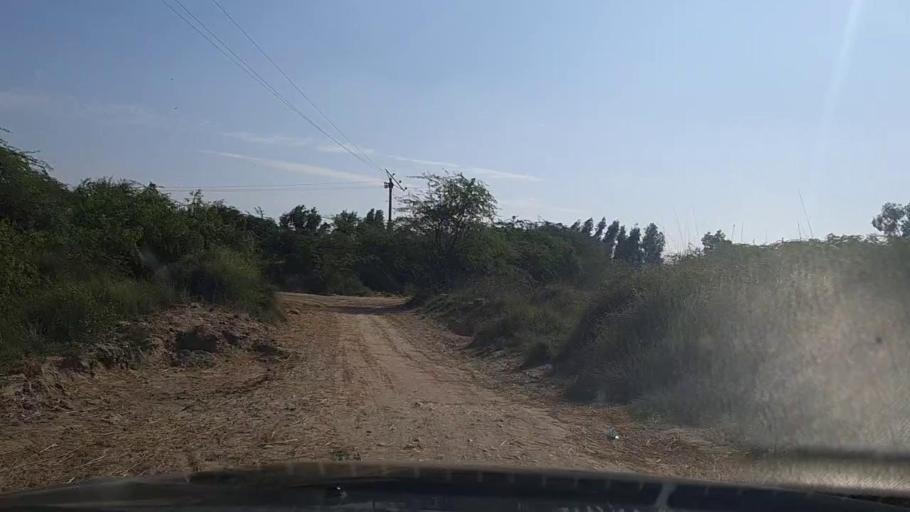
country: PK
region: Sindh
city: Thatta
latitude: 24.7110
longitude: 67.7831
